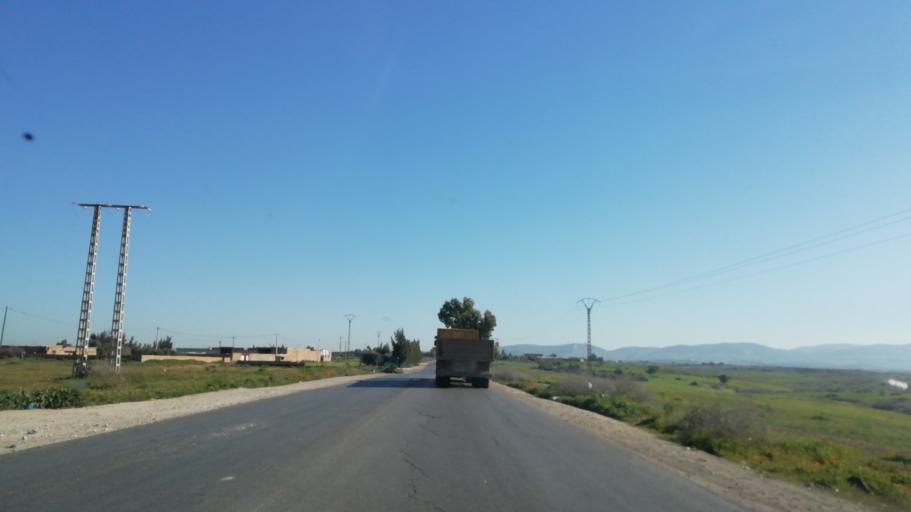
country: DZ
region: Relizane
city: Zemoura
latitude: 35.7516
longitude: 0.6863
